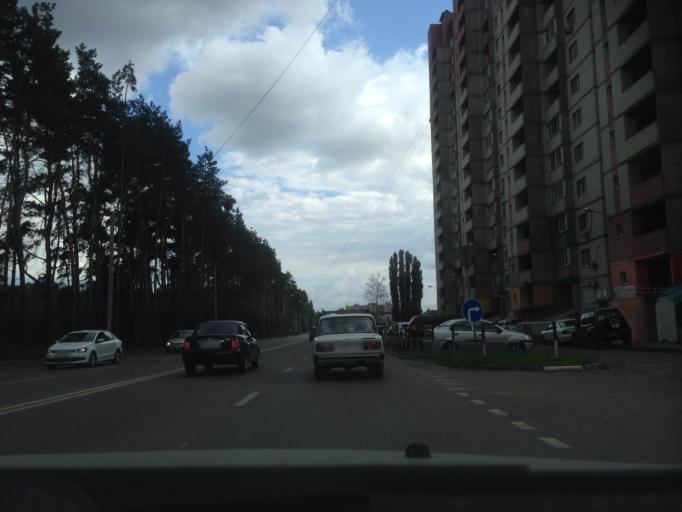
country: RU
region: Voronezj
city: Podgornoye
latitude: 51.7265
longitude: 39.1886
